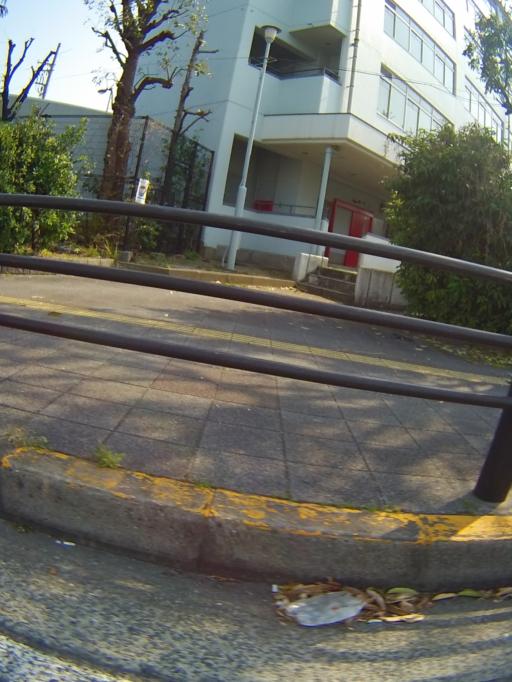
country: JP
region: Osaka
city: Osaka-shi
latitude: 34.6530
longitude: 135.4868
